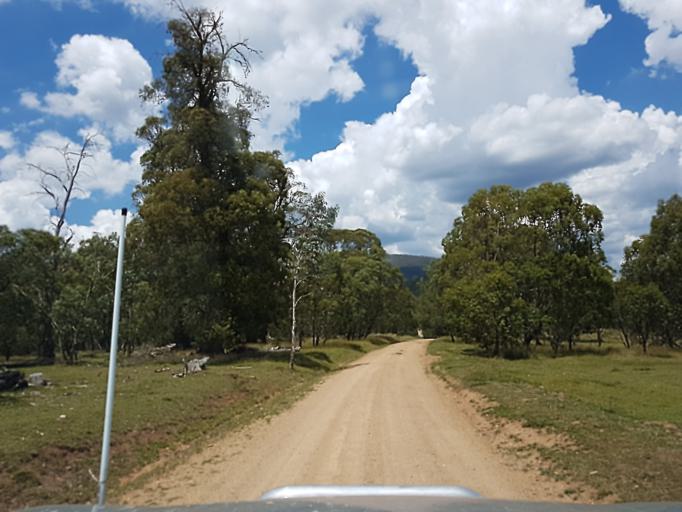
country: AU
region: New South Wales
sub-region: Snowy River
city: Jindabyne
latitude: -36.8935
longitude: 148.0887
